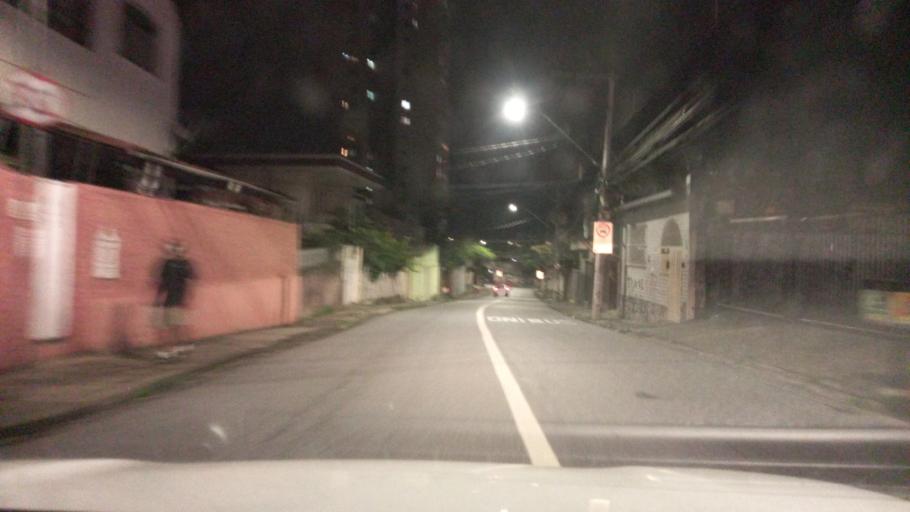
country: BR
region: Minas Gerais
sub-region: Belo Horizonte
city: Belo Horizonte
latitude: -19.9116
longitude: -43.9619
